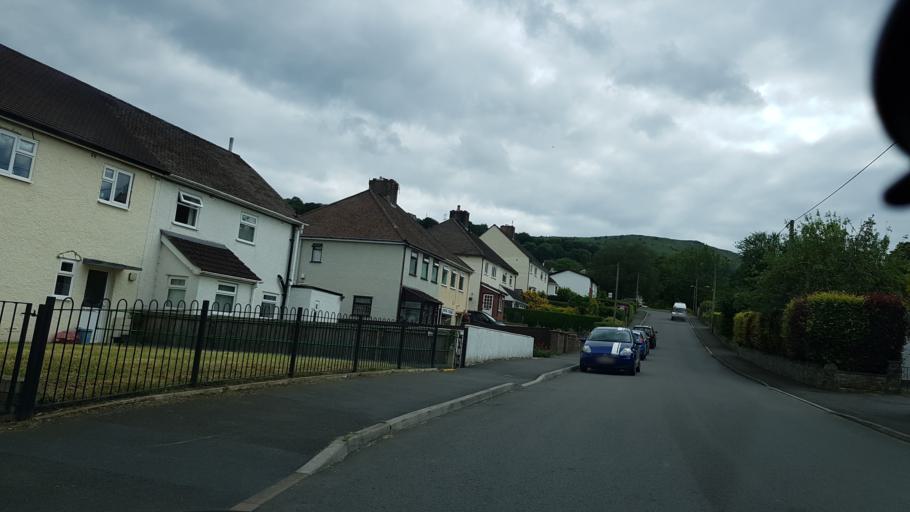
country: GB
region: Wales
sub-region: Monmouthshire
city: Gilwern
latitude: 51.8270
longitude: -3.0937
